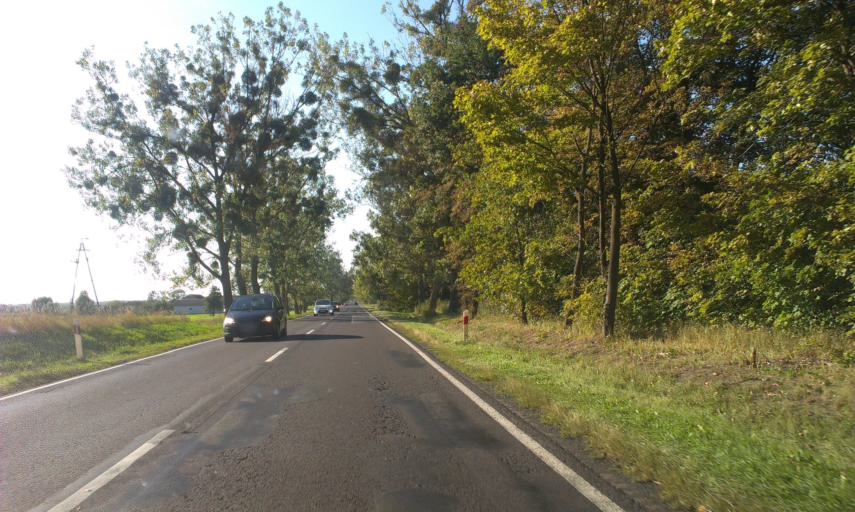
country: PL
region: Kujawsko-Pomorskie
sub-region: Powiat swiecki
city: Drzycim
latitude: 53.4216
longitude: 18.3398
